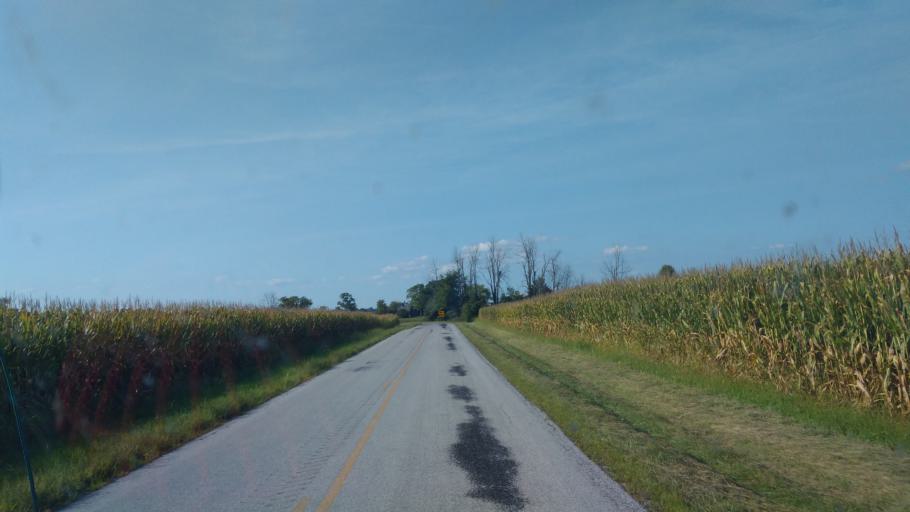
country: US
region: Ohio
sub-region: Hardin County
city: Kenton
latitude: 40.7330
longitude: -83.5746
